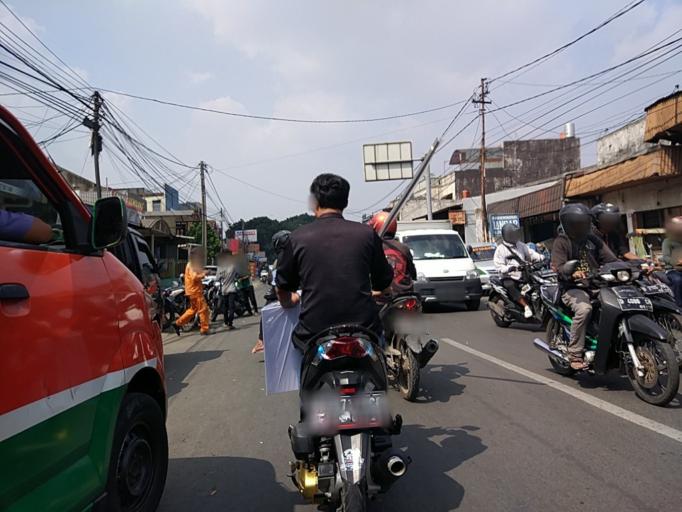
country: ID
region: West Java
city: Bandung
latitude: -6.9220
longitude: 107.5863
